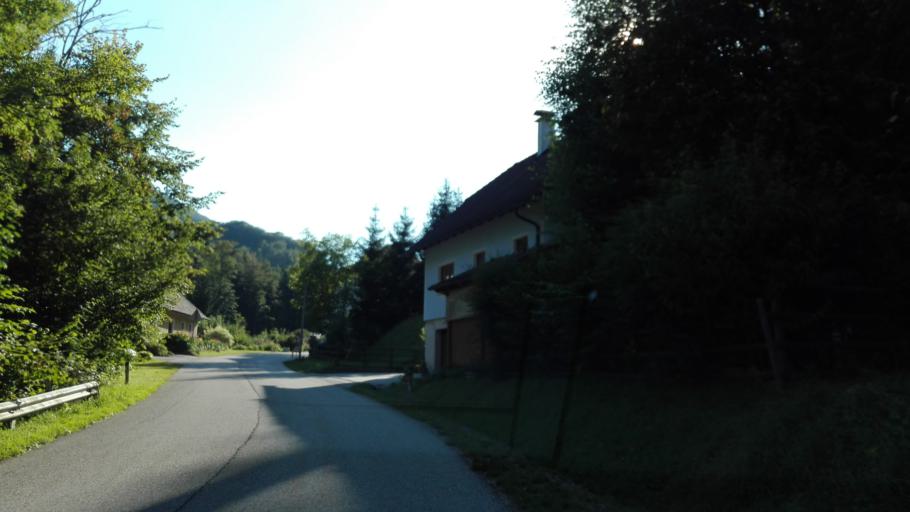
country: AT
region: Lower Austria
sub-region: Politischer Bezirk Sankt Polten
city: Stossing
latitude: 48.0853
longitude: 15.8475
